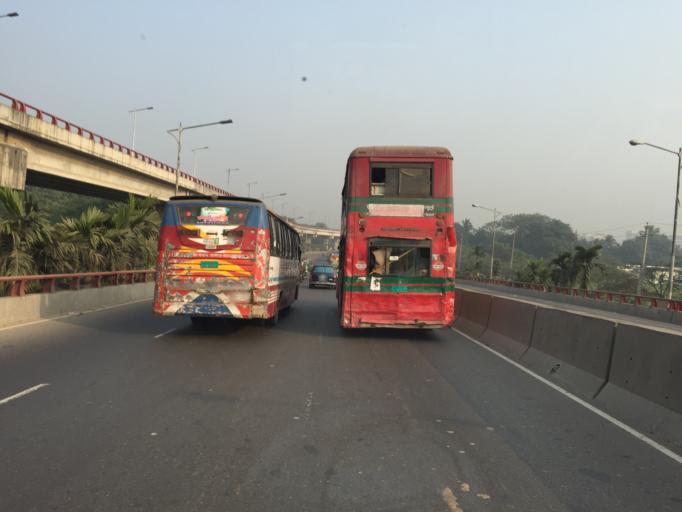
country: BD
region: Dhaka
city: Paltan
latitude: 23.8120
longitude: 90.4037
